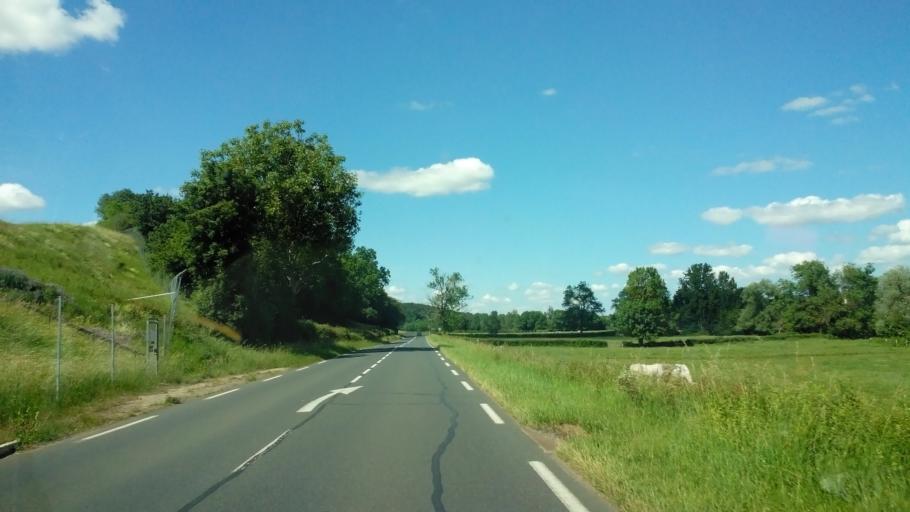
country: FR
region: Bourgogne
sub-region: Departement de Saone-et-Loire
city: Cluny
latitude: 46.4653
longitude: 4.6697
